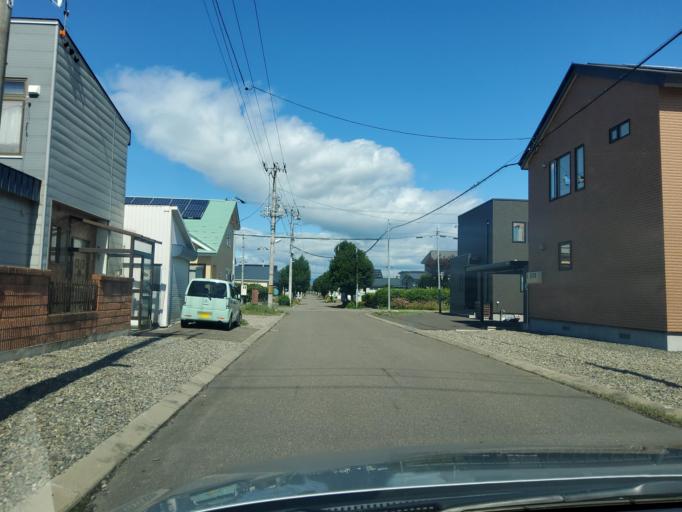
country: JP
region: Hokkaido
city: Otofuke
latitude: 42.9584
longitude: 143.1920
